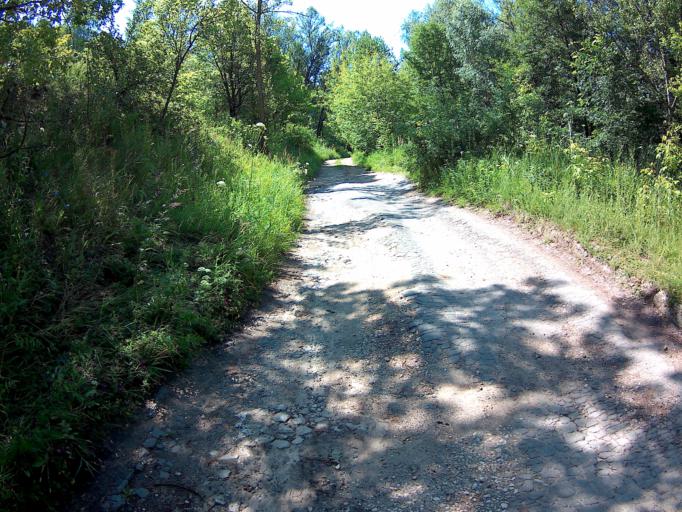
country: RU
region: Nizjnij Novgorod
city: Nizhniy Novgorod
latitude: 56.2679
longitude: 43.9709
